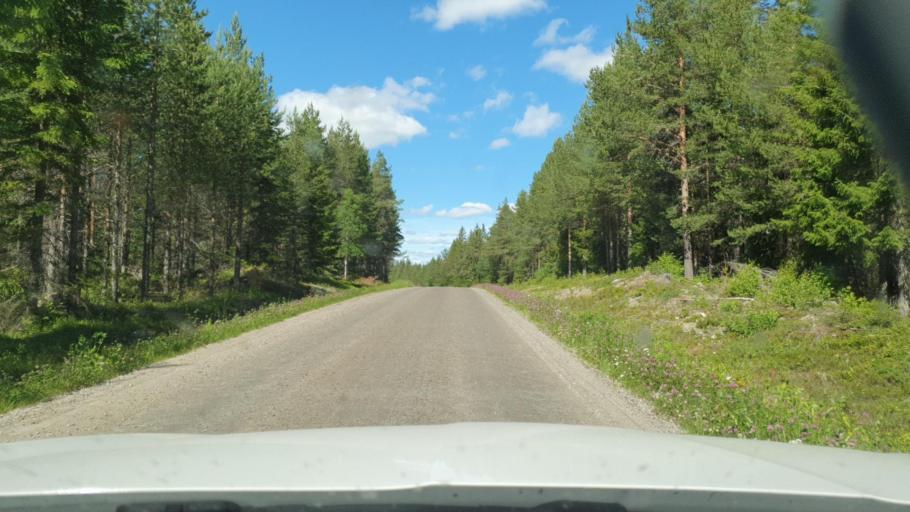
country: SE
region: Vaesterbotten
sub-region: Skelleftea Kommun
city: Byske
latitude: 65.1387
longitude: 21.1843
